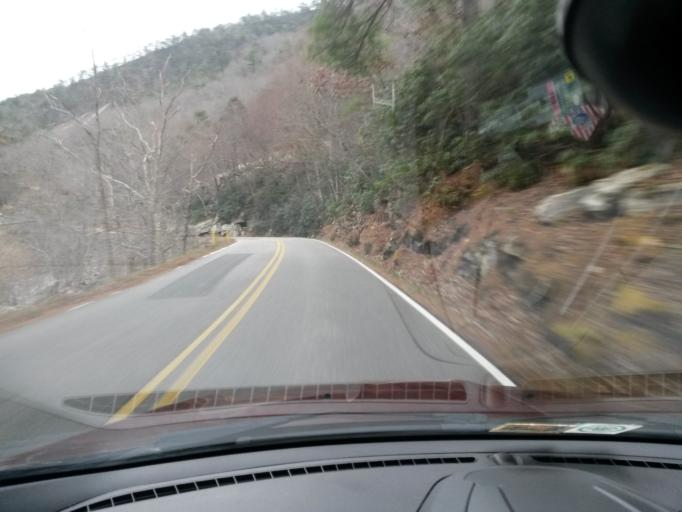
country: US
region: Virginia
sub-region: Rockbridge County
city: East Lexington
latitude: 37.9288
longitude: -79.4537
